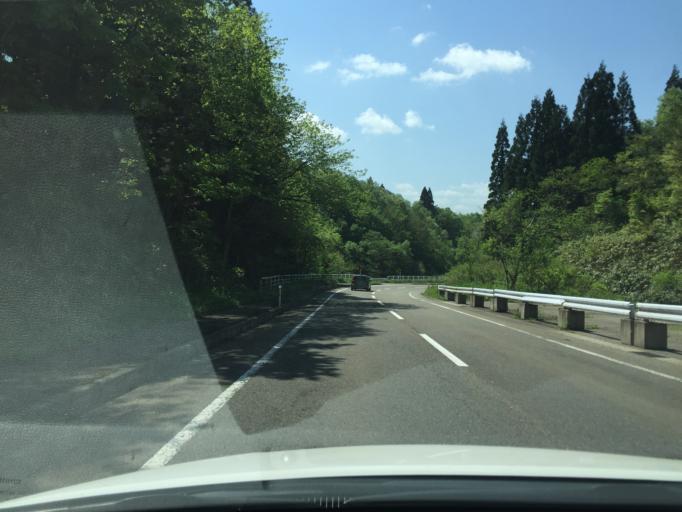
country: JP
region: Niigata
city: Kamo
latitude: 37.5817
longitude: 139.0937
